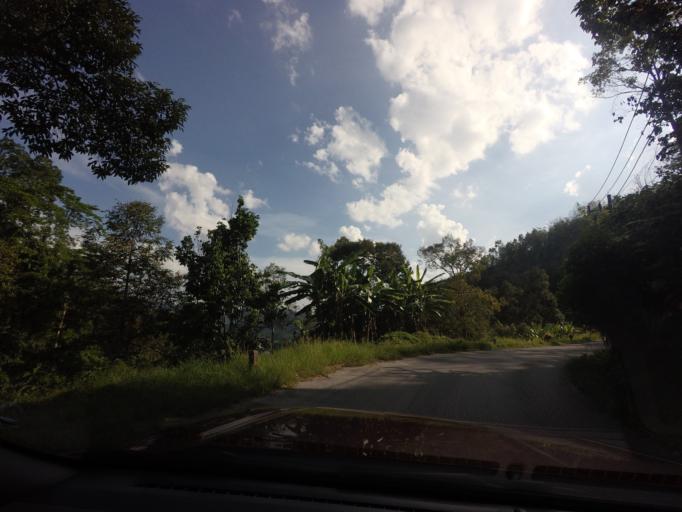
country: TH
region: Yala
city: Than To
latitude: 6.1406
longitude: 101.2970
